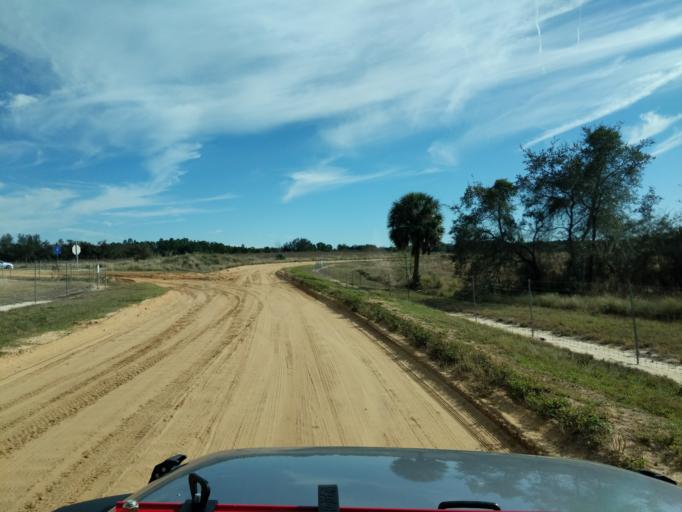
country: US
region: Florida
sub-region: Lake County
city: Clermont
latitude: 28.4817
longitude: -81.7141
